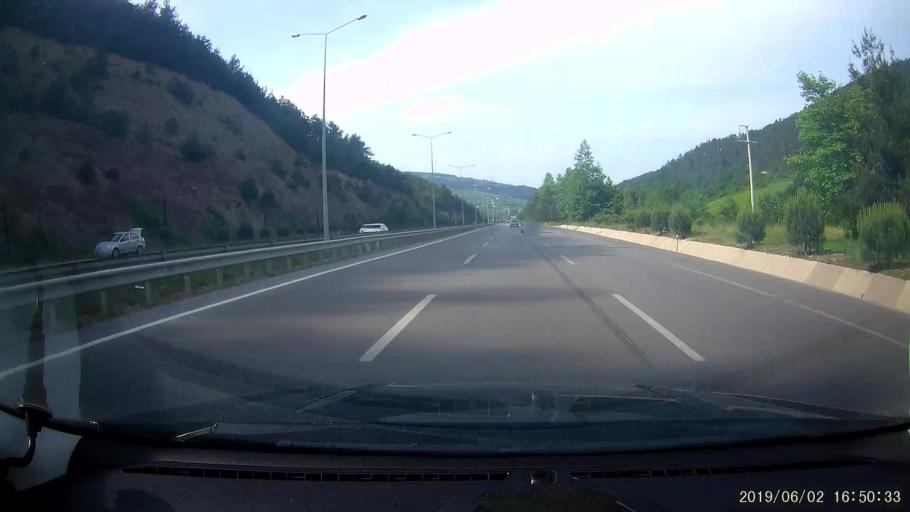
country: TR
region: Samsun
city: Taflan
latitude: 41.2571
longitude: 36.1739
